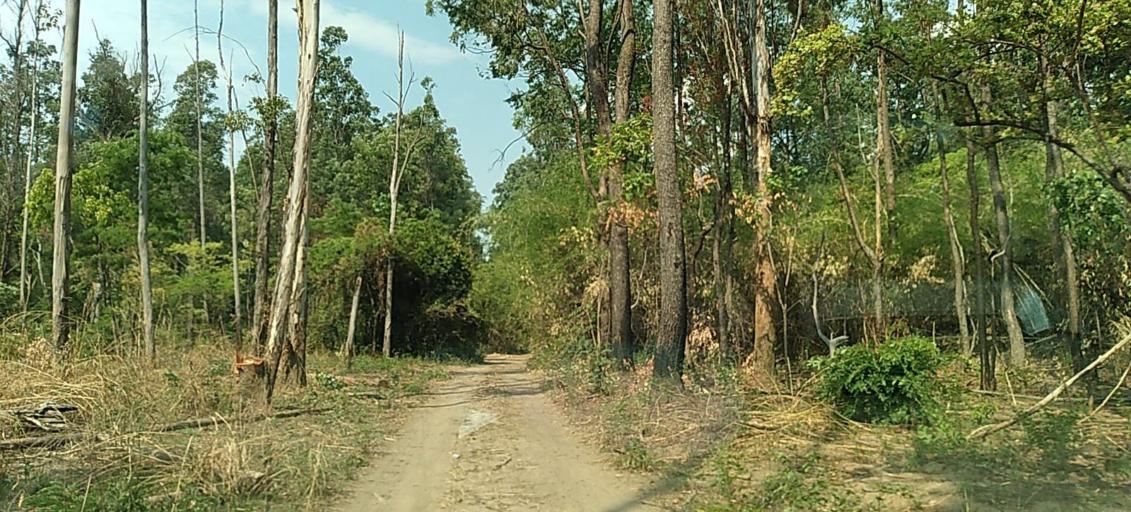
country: ZM
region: Copperbelt
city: Chingola
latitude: -12.7372
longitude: 27.7574
